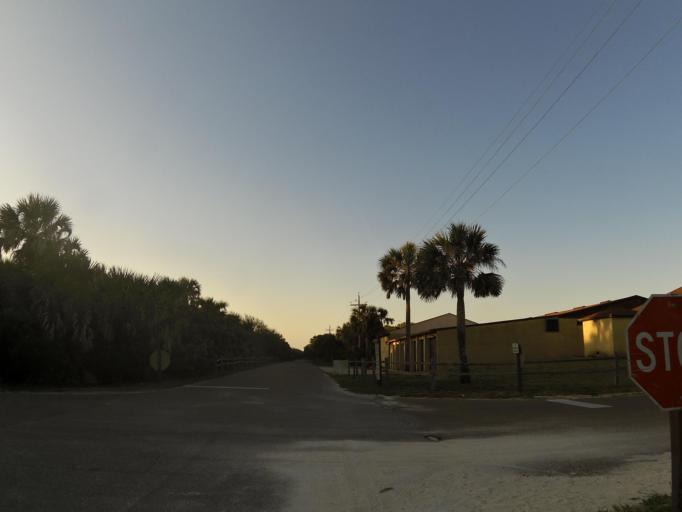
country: US
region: Florida
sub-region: Duval County
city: Atlantic Beach
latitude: 30.3663
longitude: -81.3997
